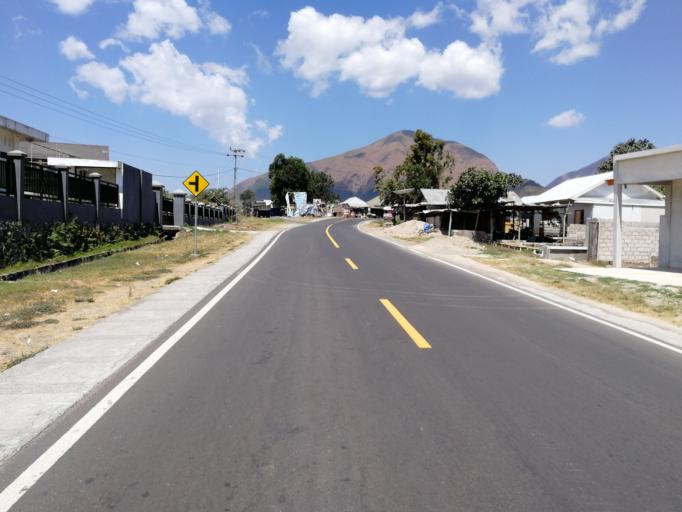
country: ID
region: West Nusa Tenggara
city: Sembalunlawang
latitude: -8.3581
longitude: 116.5221
